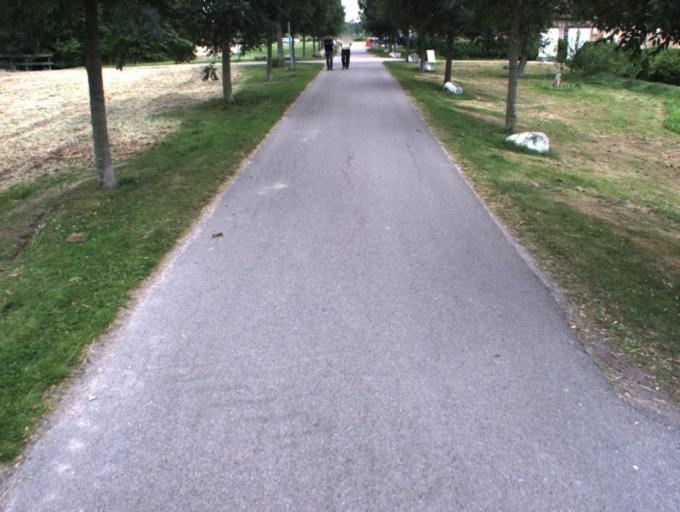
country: SE
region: Skane
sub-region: Helsingborg
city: Rydeback
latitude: 55.9690
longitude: 12.7609
